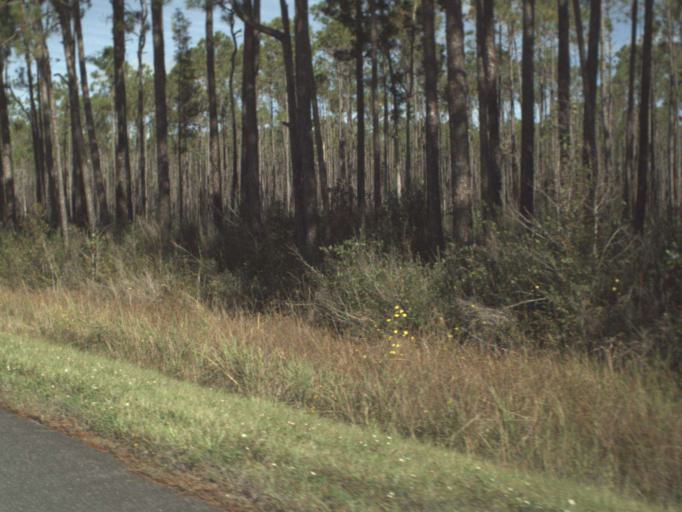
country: US
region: Florida
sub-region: Franklin County
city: Eastpoint
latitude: 29.8253
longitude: -84.9142
